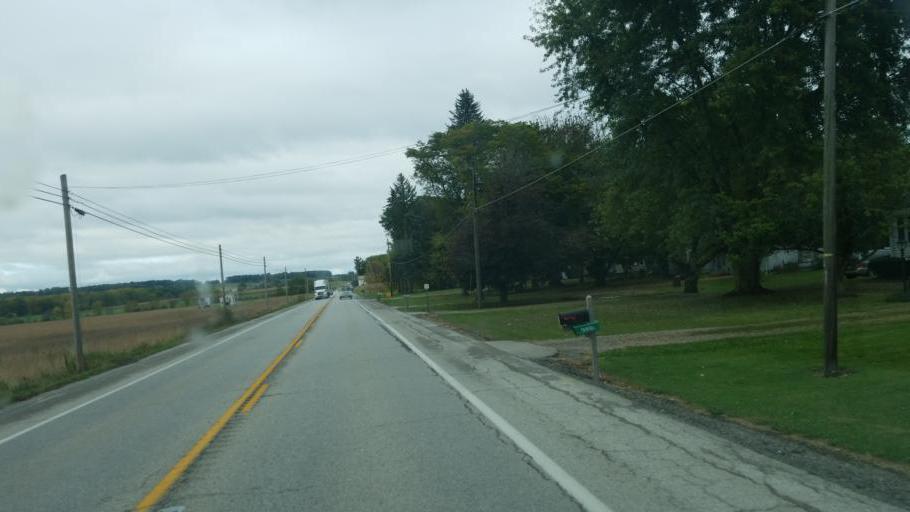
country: US
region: Ohio
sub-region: Wayne County
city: Apple Creek
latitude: 40.7567
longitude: -81.8700
